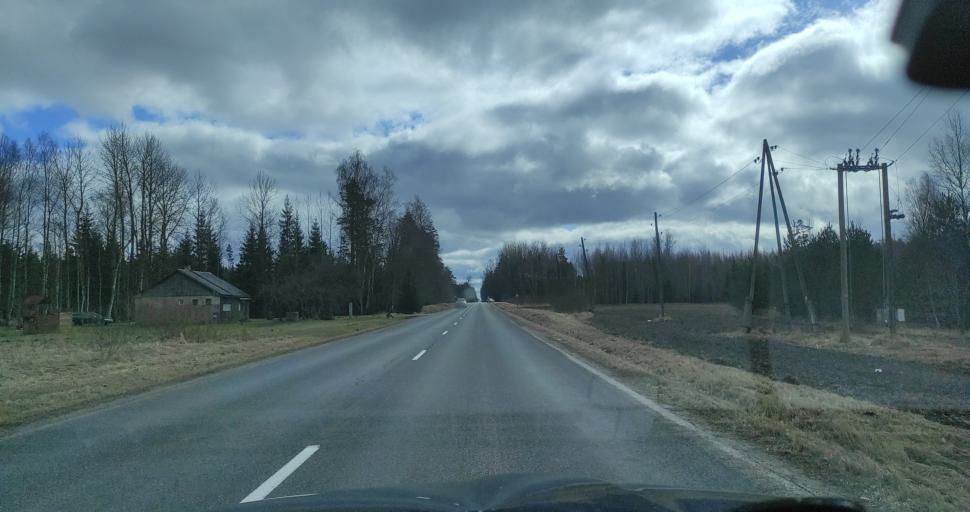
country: LV
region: Talsu Rajons
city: Stende
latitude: 57.1274
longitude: 22.5376
